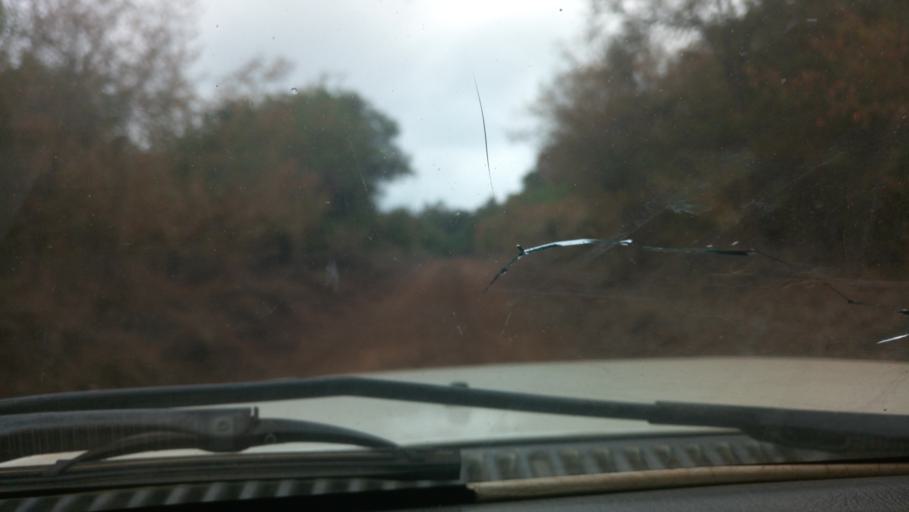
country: KE
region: Nairobi Area
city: Nairobi
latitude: -1.3685
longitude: 36.7715
